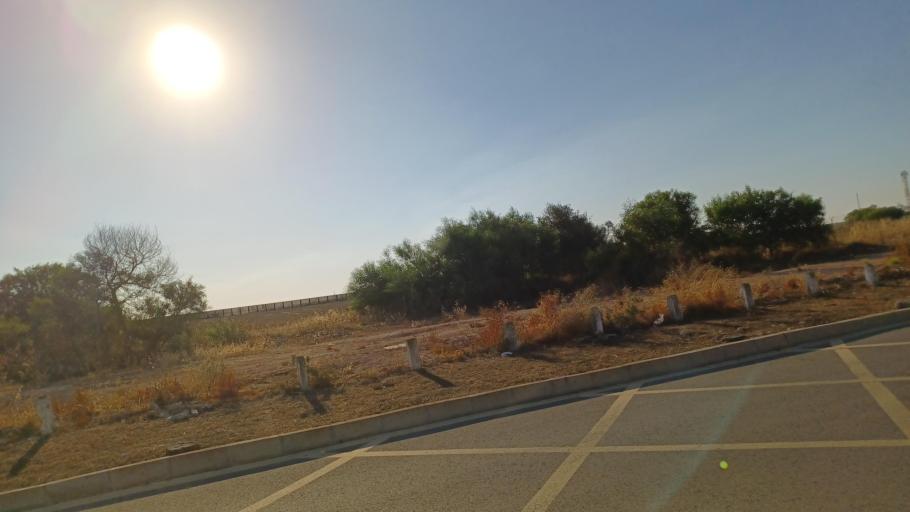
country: CY
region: Larnaka
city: Xylotymbou
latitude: 34.9969
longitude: 33.7421
